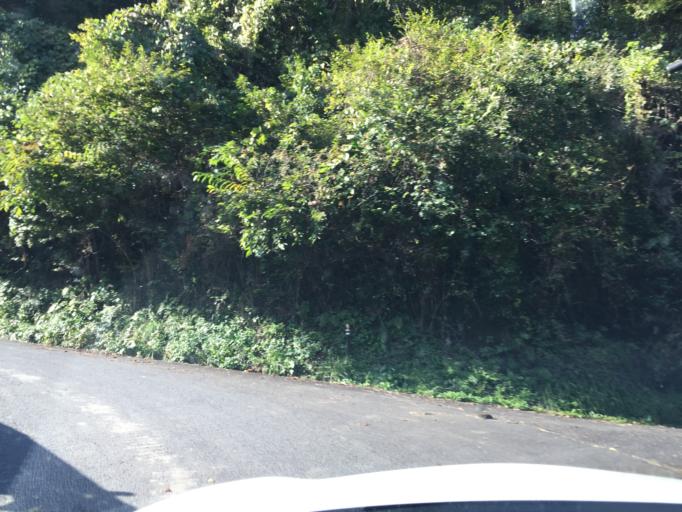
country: JP
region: Fukushima
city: Ishikawa
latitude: 37.1691
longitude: 140.4953
